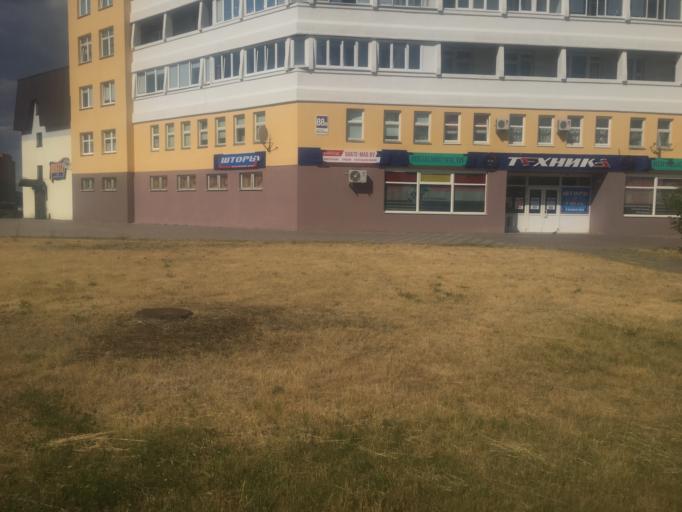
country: BY
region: Grodnenskaya
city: Hrodna
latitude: 53.6534
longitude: 23.8517
